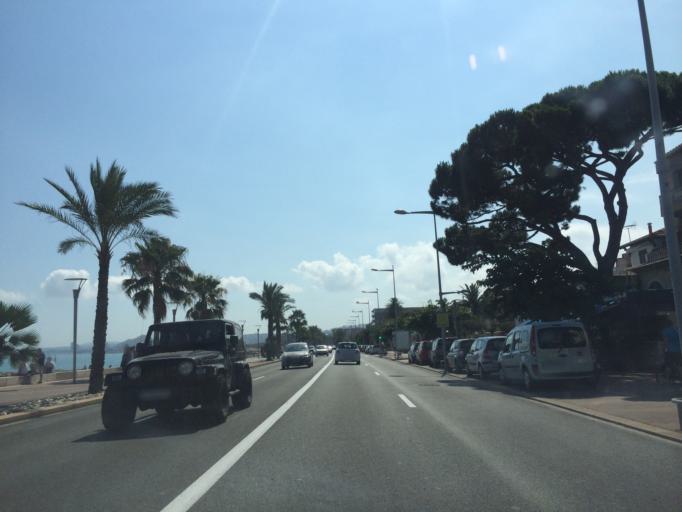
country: FR
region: Provence-Alpes-Cote d'Azur
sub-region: Departement des Alpes-Maritimes
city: Cagnes-sur-Mer
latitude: 43.6562
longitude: 7.1627
